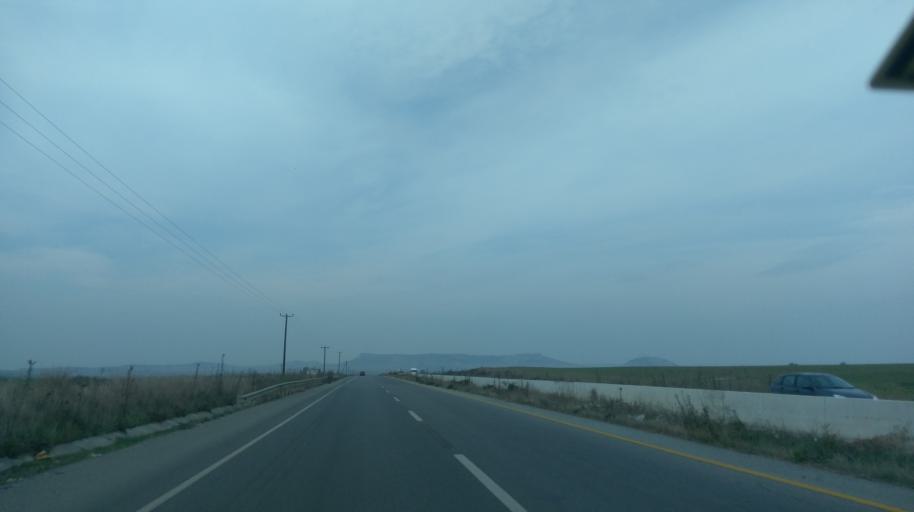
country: CY
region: Lefkosia
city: Mammari
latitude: 35.2119
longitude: 33.2066
